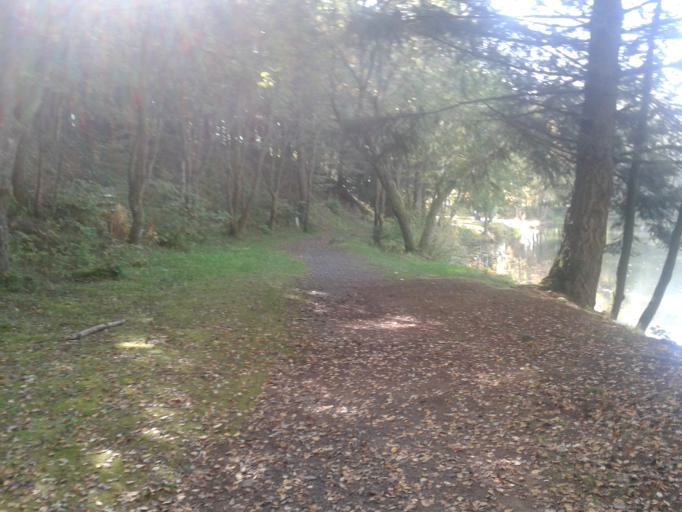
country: DE
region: Bavaria
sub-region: Regierungsbezirk Unterfranken
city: Oberelsbach
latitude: 50.4561
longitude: 10.0549
